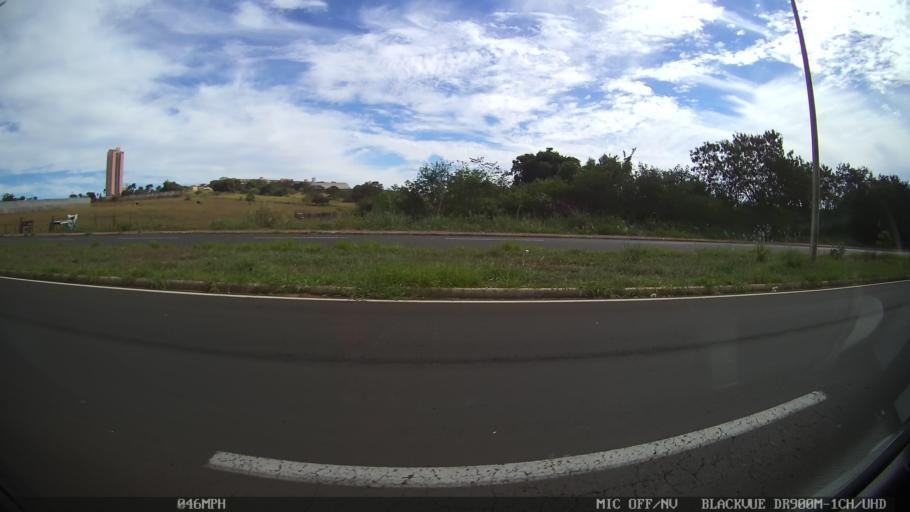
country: BR
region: Sao Paulo
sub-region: Catanduva
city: Catanduva
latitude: -21.1511
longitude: -48.9514
